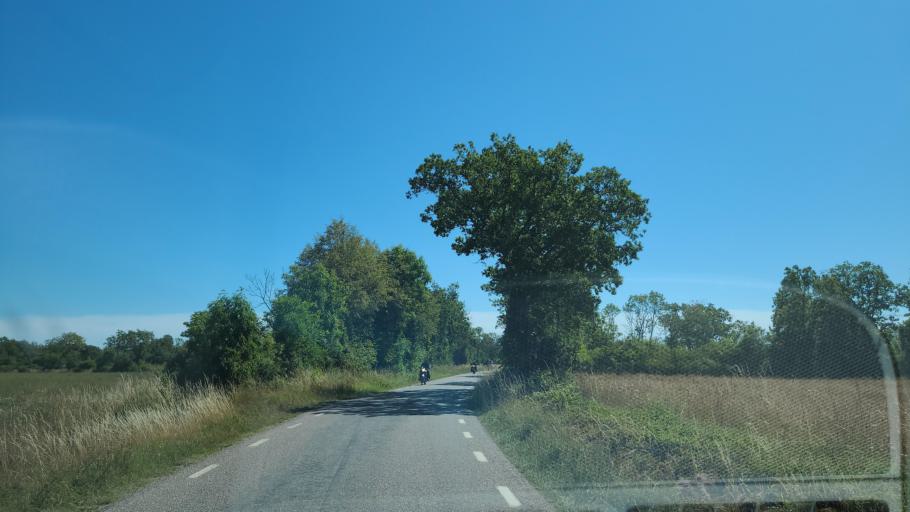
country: SE
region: Kalmar
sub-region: Borgholms Kommun
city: Borgholm
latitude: 56.7461
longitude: 16.6617
